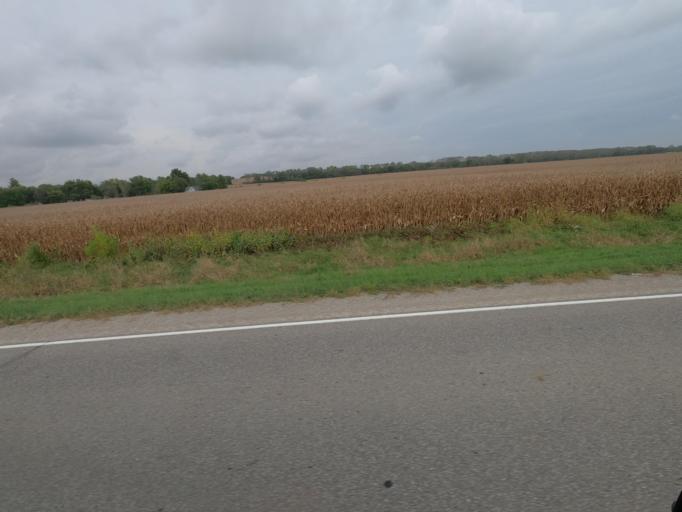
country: US
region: Iowa
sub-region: Wapello County
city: Ottumwa
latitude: 40.9117
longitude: -92.2119
